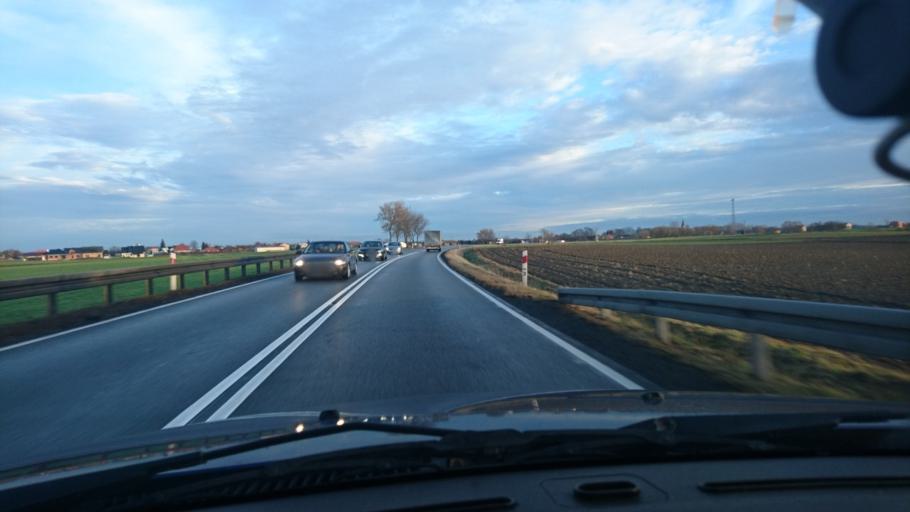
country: PL
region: Greater Poland Voivodeship
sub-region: Powiat kepinski
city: Opatow
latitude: 51.2210
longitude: 18.1326
